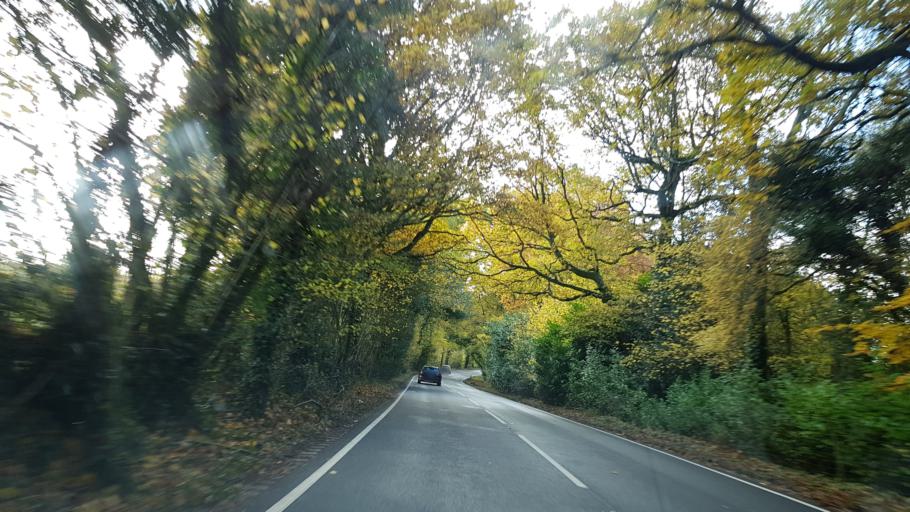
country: GB
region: England
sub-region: Surrey
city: Haslemere
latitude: 51.1213
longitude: -0.6742
